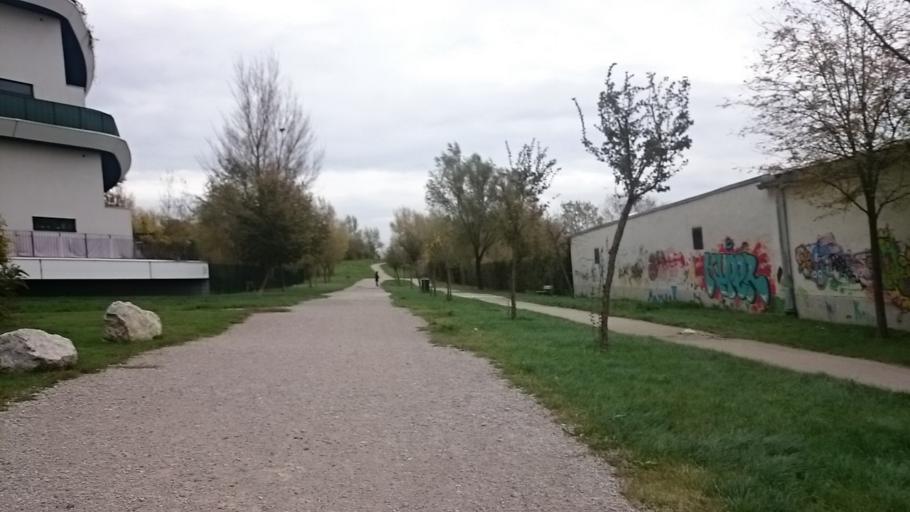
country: AT
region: Lower Austria
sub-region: Politischer Bezirk Modling
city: Vosendorf
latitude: 48.1681
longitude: 16.3419
